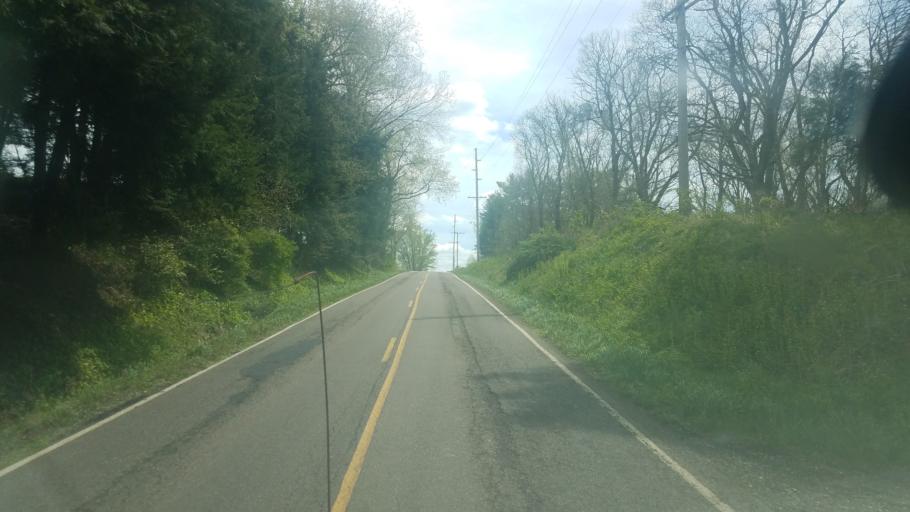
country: US
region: Ohio
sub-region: Wayne County
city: Wooster
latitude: 40.7375
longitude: -81.9442
